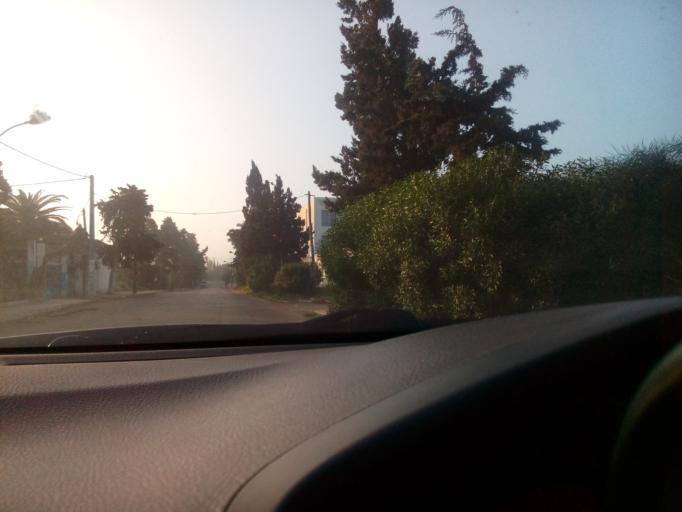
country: DZ
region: Oran
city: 'Ain el Turk
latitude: 35.7040
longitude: -0.8926
